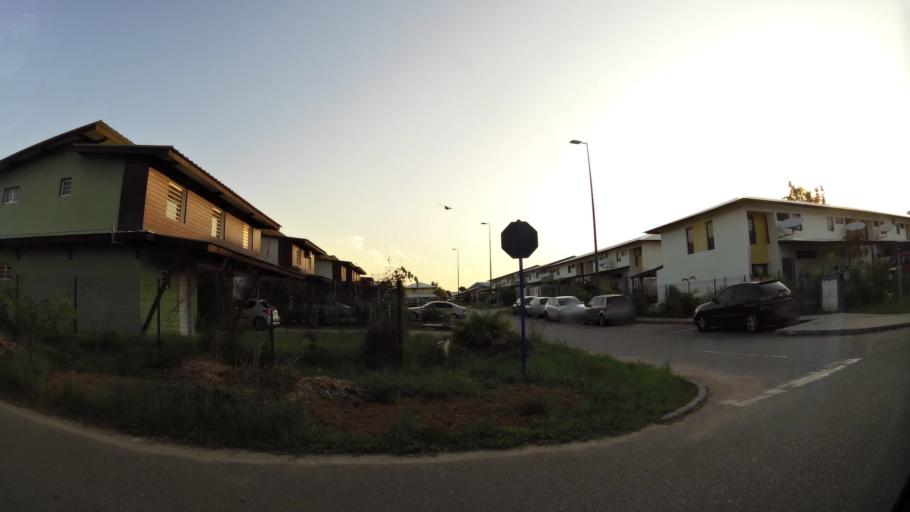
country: GF
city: Macouria
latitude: 4.9325
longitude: -52.4112
